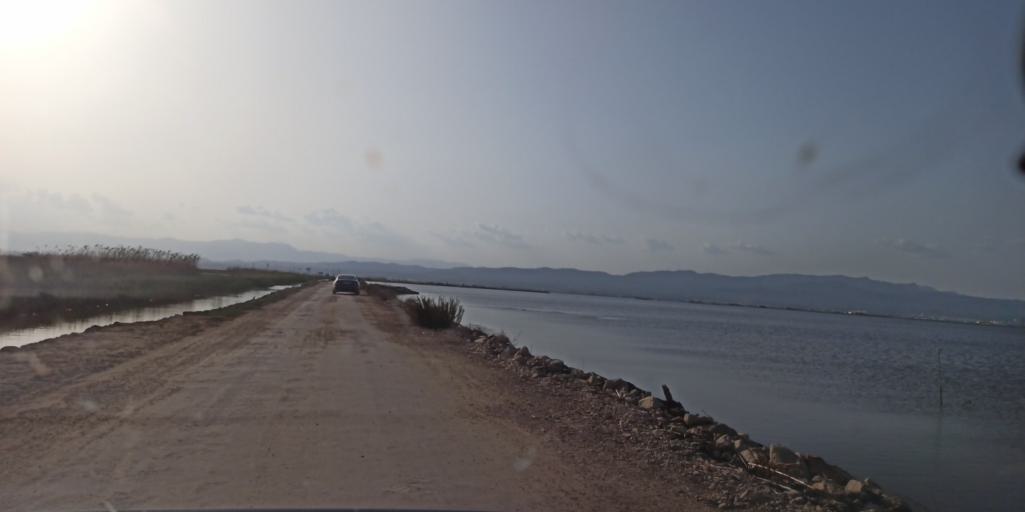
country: ES
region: Catalonia
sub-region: Provincia de Tarragona
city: Deltebre
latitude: 40.7645
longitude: 0.7490
